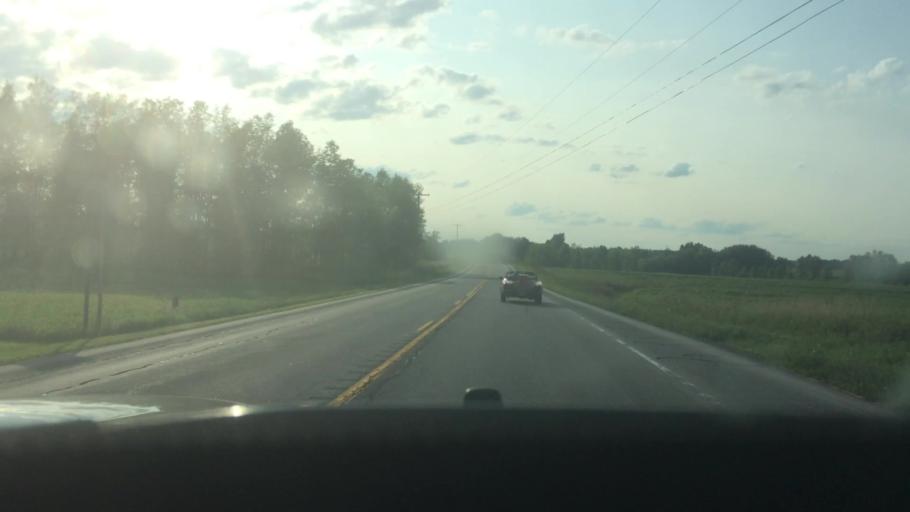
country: US
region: New York
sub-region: St. Lawrence County
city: Ogdensburg
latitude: 44.6593
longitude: -75.3298
